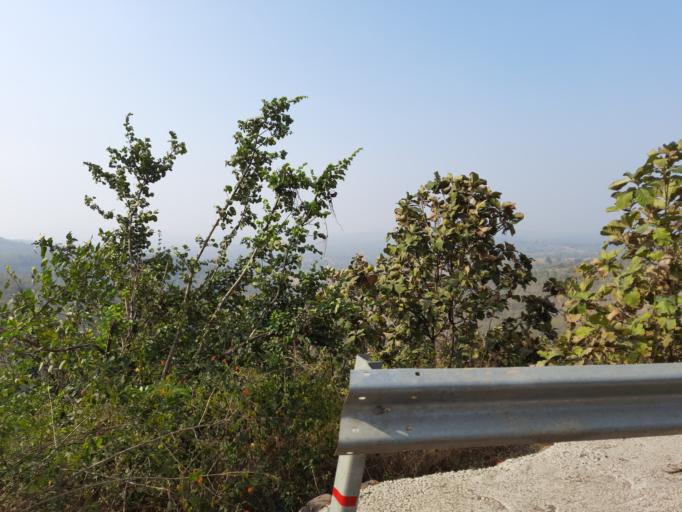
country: IN
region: Maharashtra
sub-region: Nashik Division
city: Surgana
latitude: 20.2591
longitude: 73.6172
